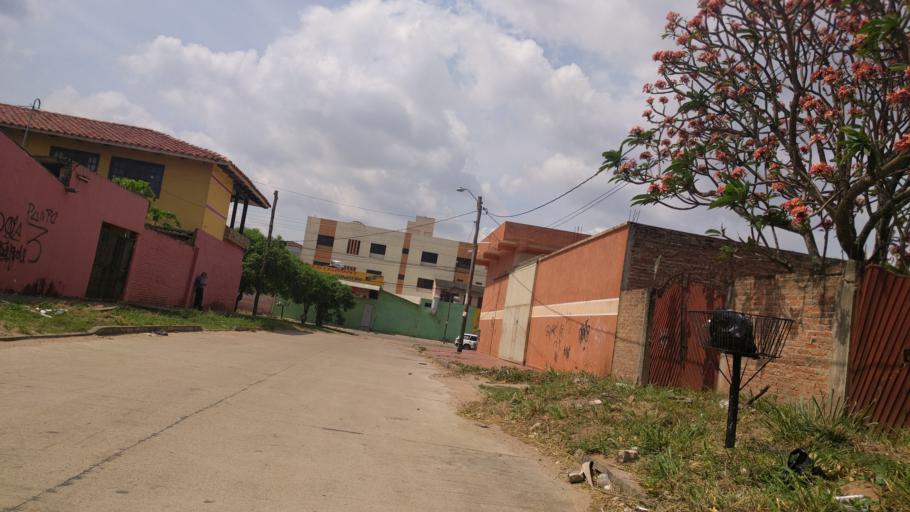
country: BO
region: Santa Cruz
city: Santa Cruz de la Sierra
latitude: -17.7918
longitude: -63.2200
